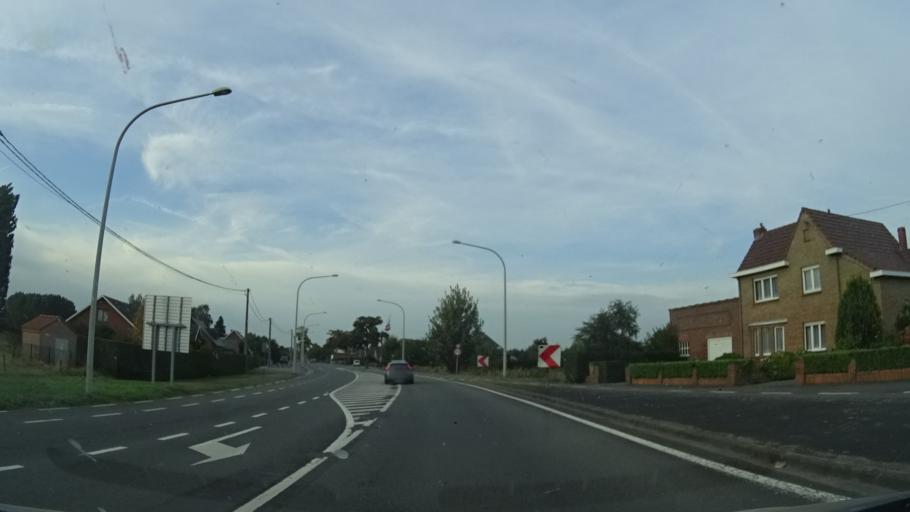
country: BE
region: Wallonia
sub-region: Province du Hainaut
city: Peruwelz
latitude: 50.5787
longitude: 3.6205
